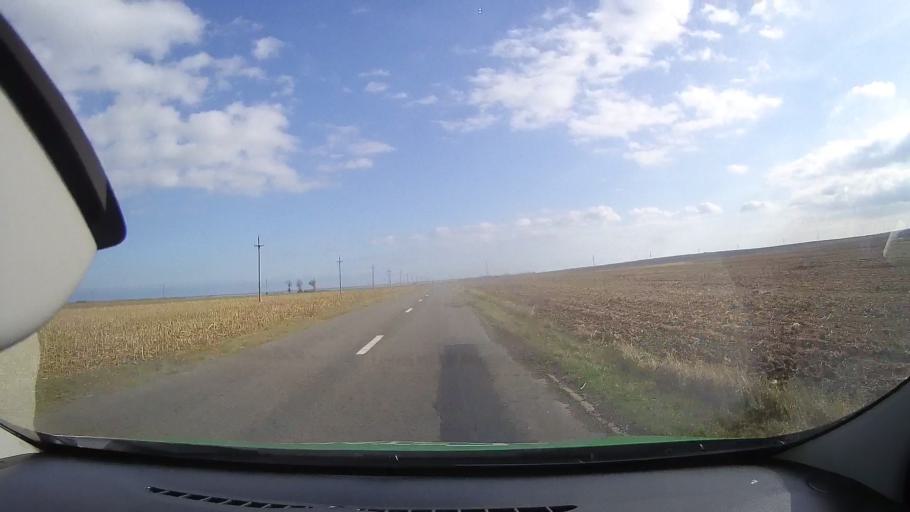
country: RO
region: Constanta
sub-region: Comuna Istria
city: Nuntasi
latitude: 44.5319
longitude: 28.6732
